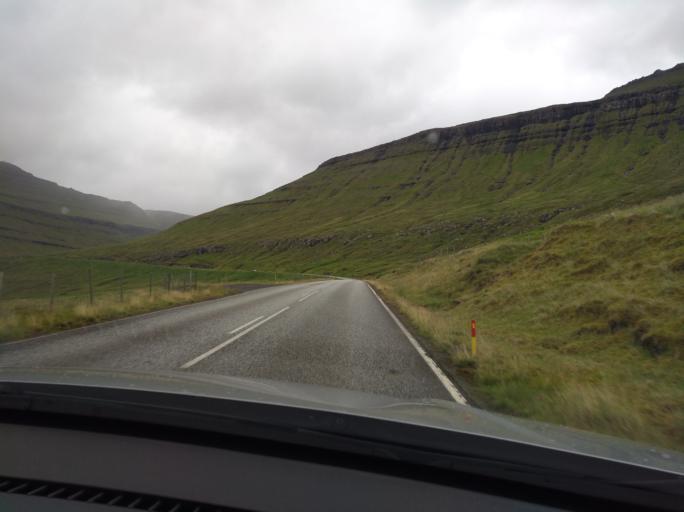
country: FO
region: Eysturoy
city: Fuglafjordur
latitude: 62.2135
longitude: -6.8631
